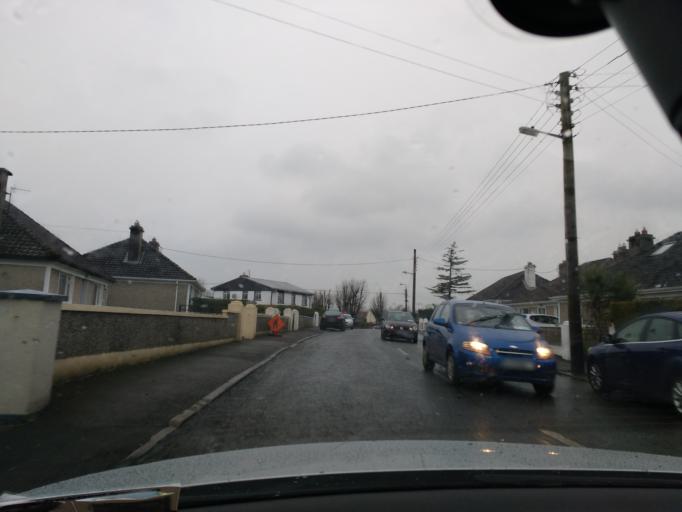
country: IE
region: Munster
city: Thurles
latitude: 52.6727
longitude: -7.8160
